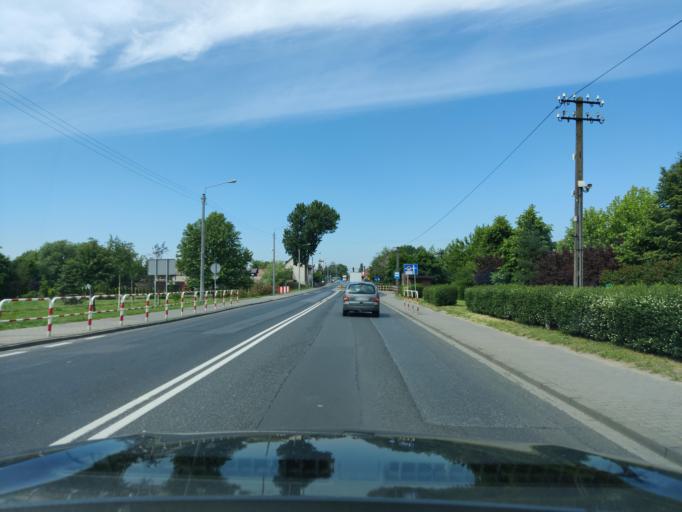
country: PL
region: Greater Poland Voivodeship
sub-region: Powiat grodziski
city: Granowo
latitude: 52.2224
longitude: 16.5321
